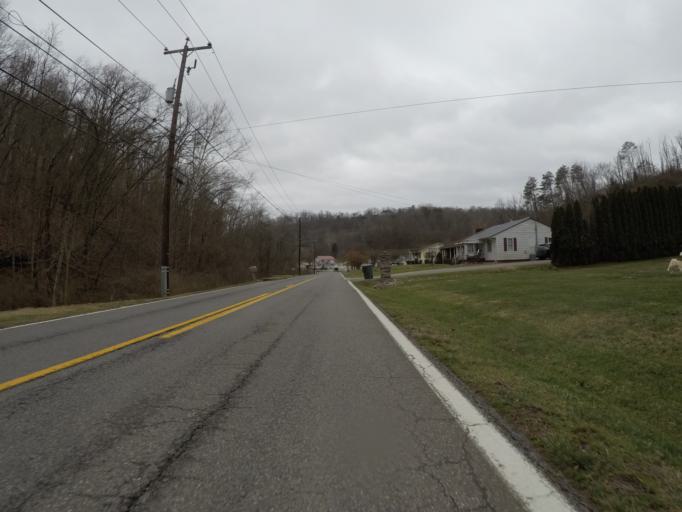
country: US
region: West Virginia
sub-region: Cabell County
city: Barboursville
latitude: 38.4354
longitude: -82.2935
